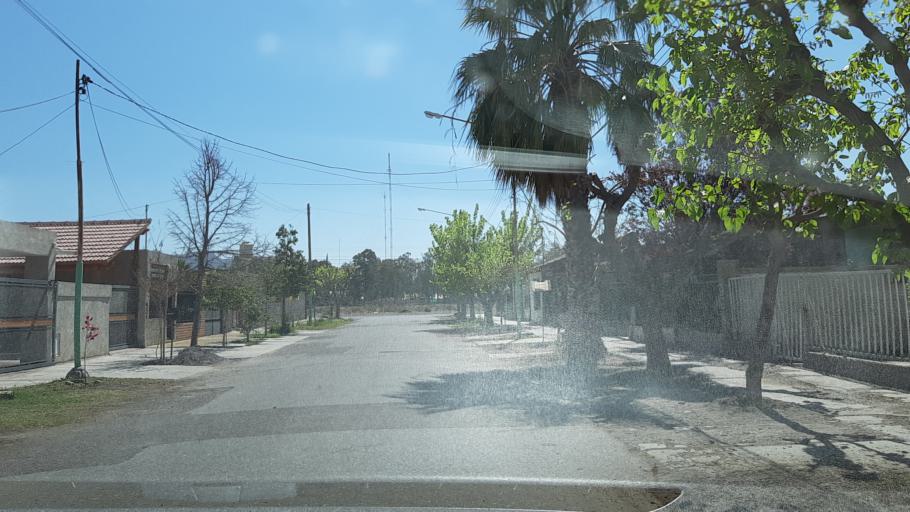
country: AR
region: San Juan
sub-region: Departamento de Rivadavia
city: Rivadavia
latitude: -31.5231
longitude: -68.6268
